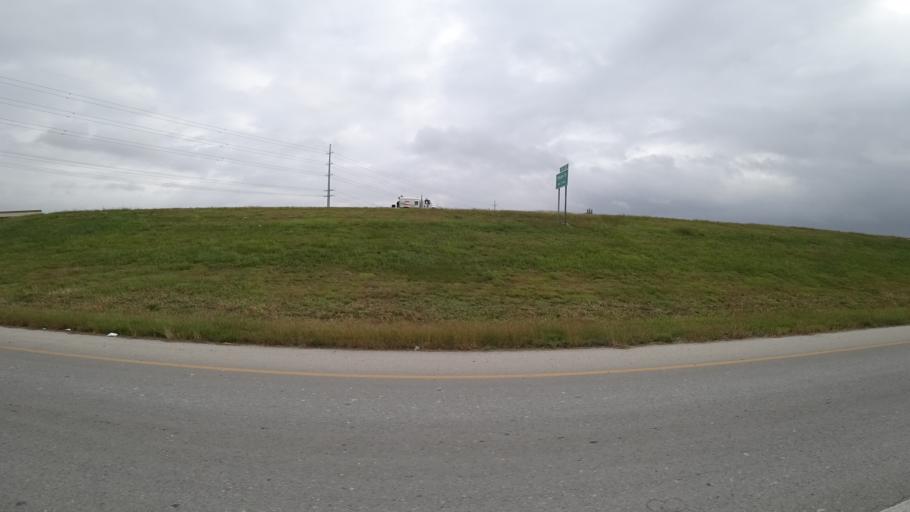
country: US
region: Texas
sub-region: Travis County
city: Pflugerville
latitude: 30.4511
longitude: -97.5951
